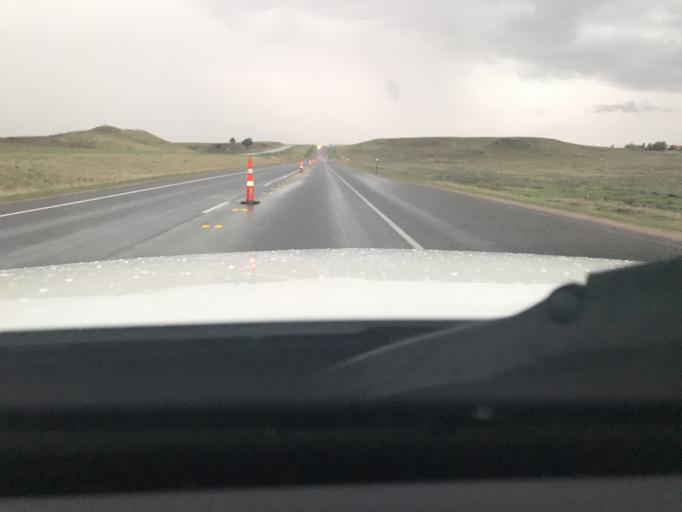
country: US
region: Wyoming
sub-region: Platte County
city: Wheatland
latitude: 42.2800
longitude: -105.0483
